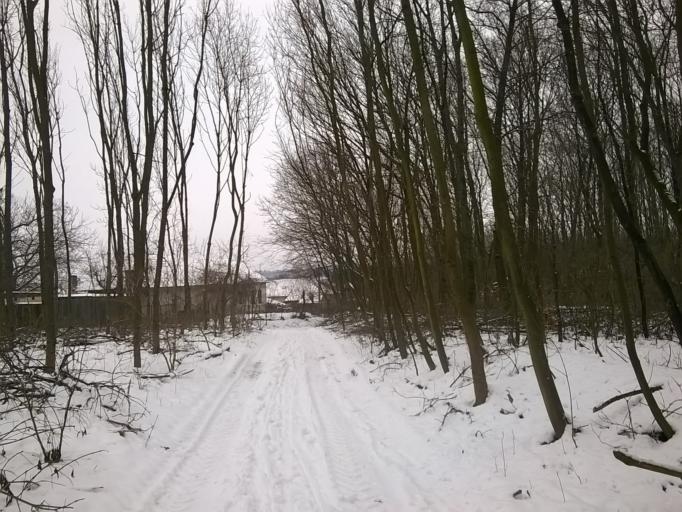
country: SK
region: Nitriansky
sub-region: Okres Nitra
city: Nitra
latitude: 48.2801
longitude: 18.0121
